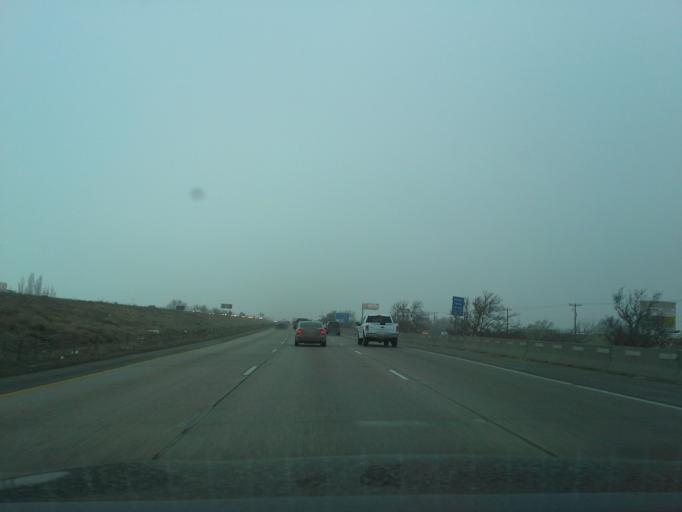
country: US
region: Utah
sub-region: Weber County
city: Roy
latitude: 41.1515
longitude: -112.0256
